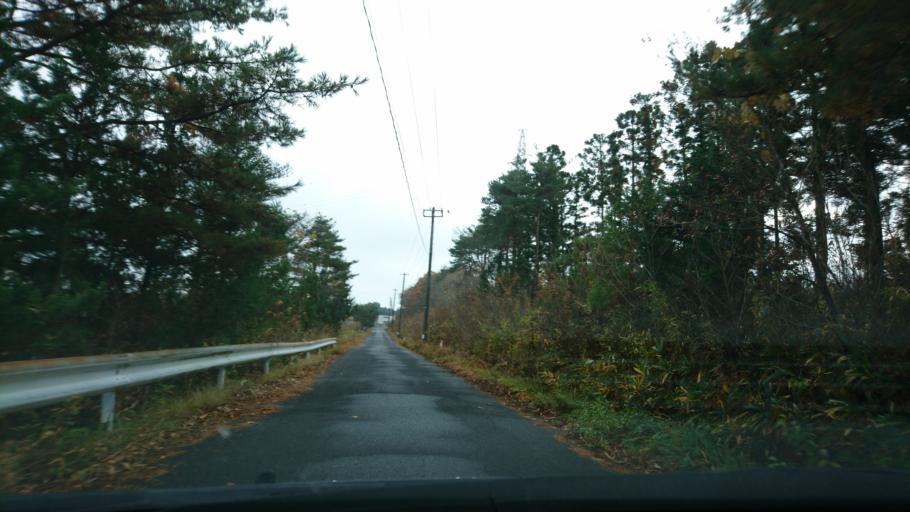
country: JP
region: Iwate
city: Ichinoseki
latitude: 38.8794
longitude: 141.1486
